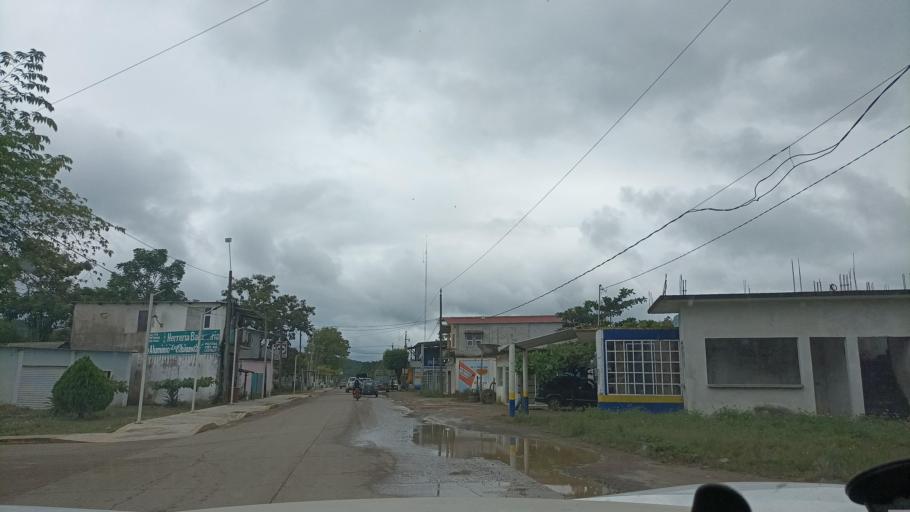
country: MX
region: Veracruz
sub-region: Uxpanapa
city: Poblado 10
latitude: 17.2801
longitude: -94.4541
